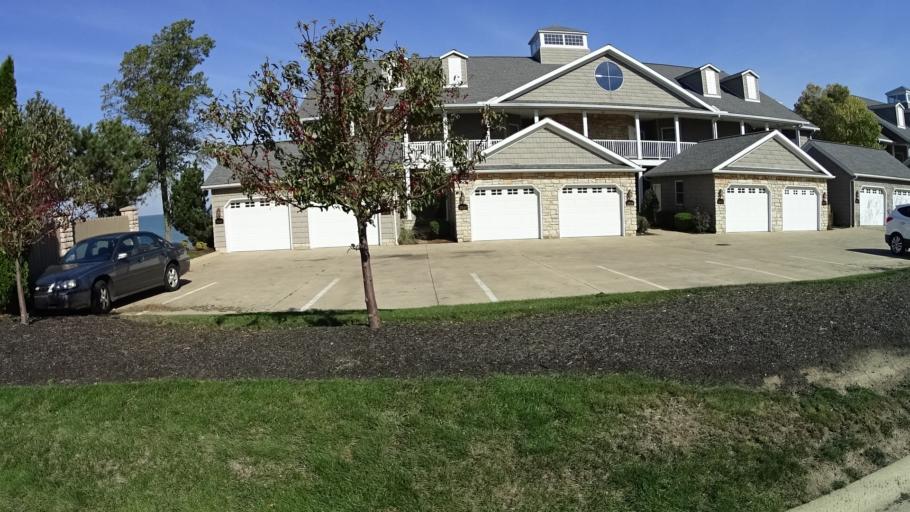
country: US
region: Ohio
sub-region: Lorain County
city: Vermilion-on-the-Lake
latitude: 41.4285
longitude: -82.3025
